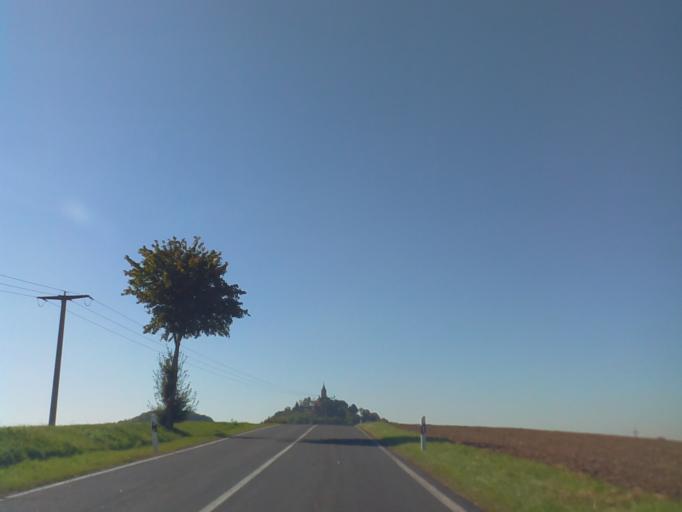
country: DE
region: Thuringia
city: Seitenroda
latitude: 50.8055
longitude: 11.6302
